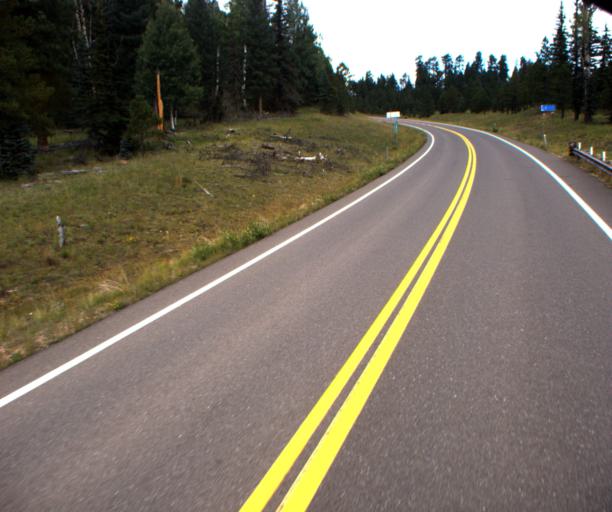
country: US
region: Arizona
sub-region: Apache County
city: Eagar
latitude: 33.9816
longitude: -109.5022
